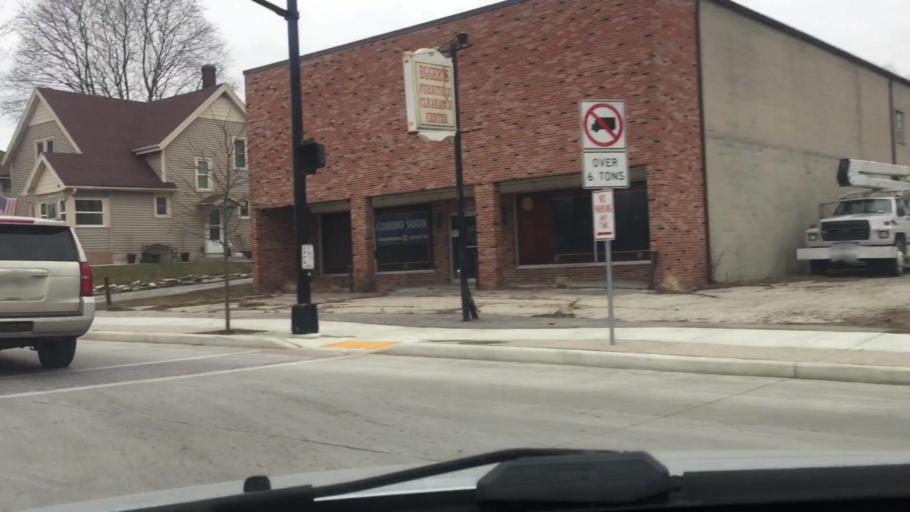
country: US
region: Wisconsin
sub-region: Waukesha County
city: Sussex
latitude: 43.1337
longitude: -88.2170
